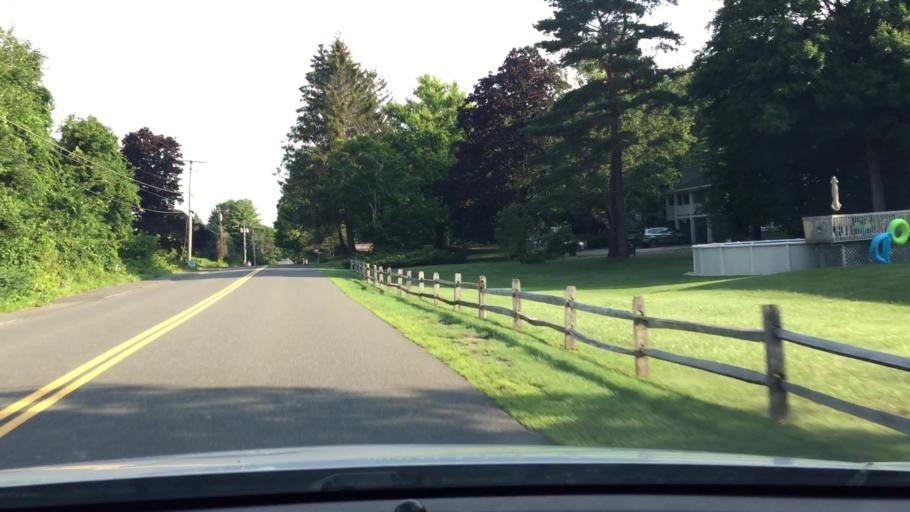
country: US
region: Massachusetts
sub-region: Berkshire County
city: Lee
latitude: 42.3152
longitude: -73.2345
